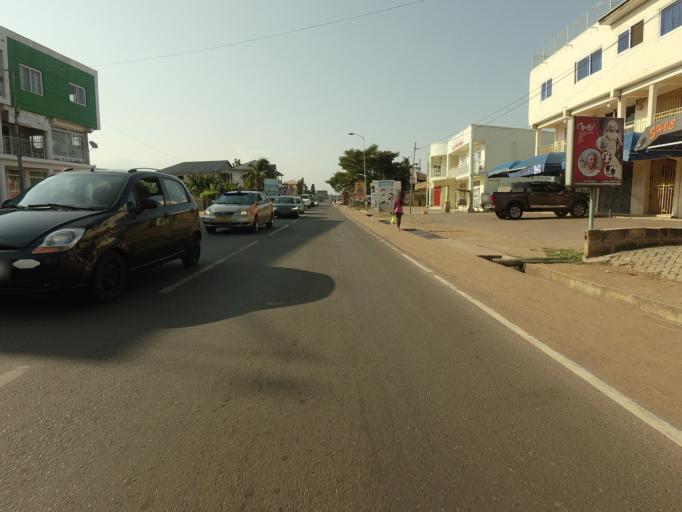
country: GH
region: Greater Accra
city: Nungua
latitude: 5.6272
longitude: -0.0762
